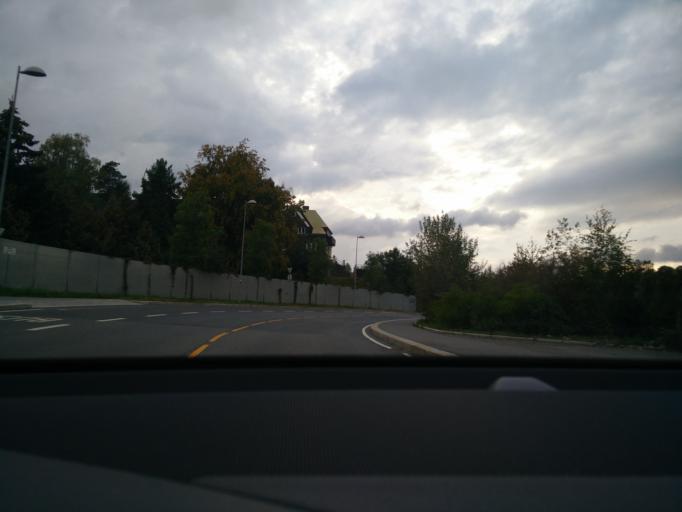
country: NO
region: Akershus
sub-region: Baerum
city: Lysaker
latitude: 59.9139
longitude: 10.6328
